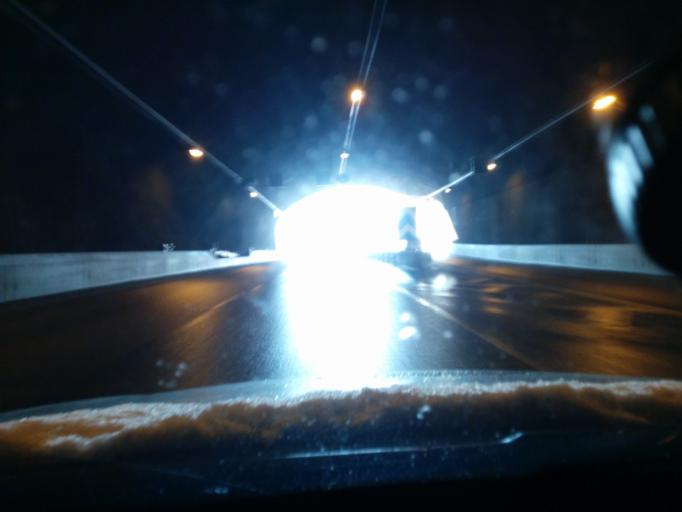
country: SE
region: Stockholm
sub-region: Sollentuna Kommun
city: Sollentuna
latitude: 59.4618
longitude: 17.9671
